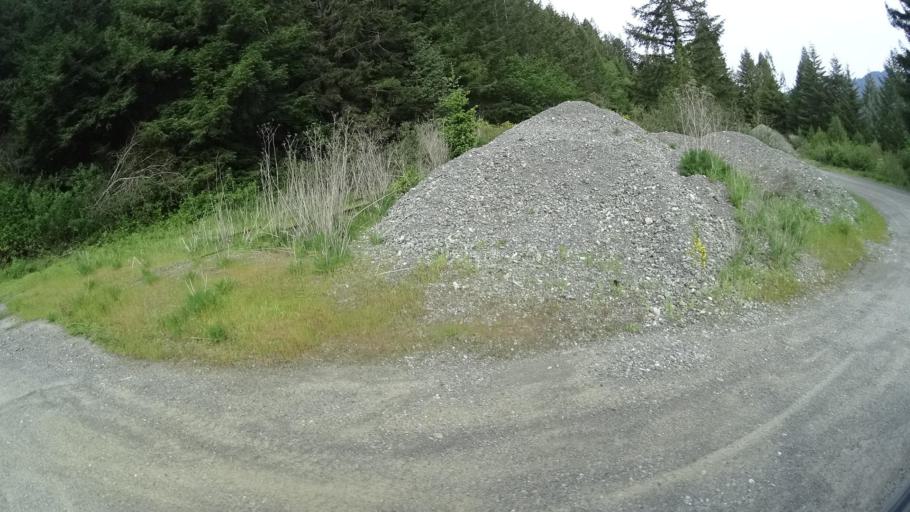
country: US
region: California
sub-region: Humboldt County
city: Redway
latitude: 40.3235
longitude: -123.8365
